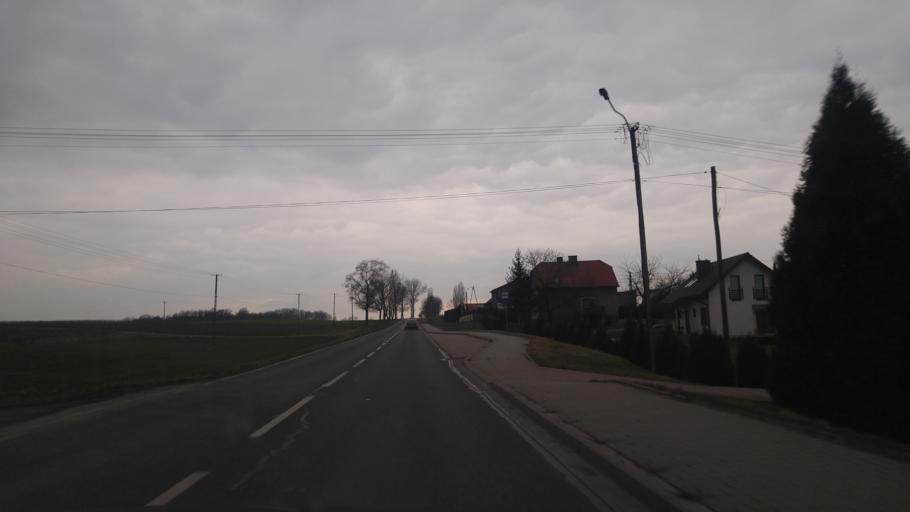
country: PL
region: Silesian Voivodeship
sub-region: Powiat pszczynski
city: Radostowice
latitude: 49.9539
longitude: 18.8923
